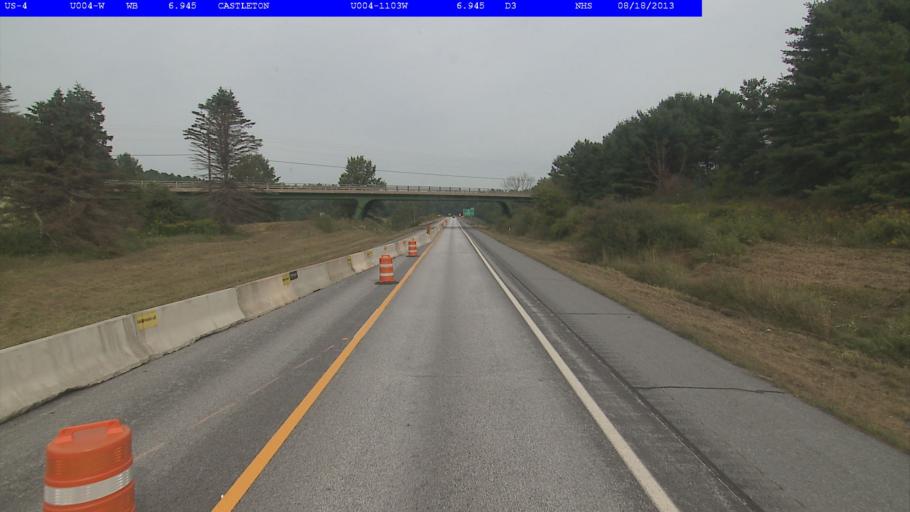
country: US
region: Vermont
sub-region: Rutland County
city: Castleton
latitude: 43.6192
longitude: -73.1807
